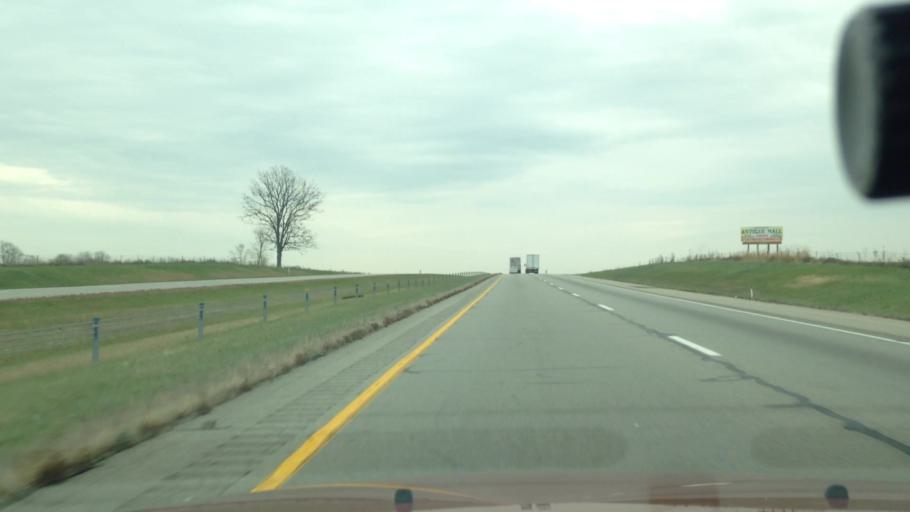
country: US
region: Indiana
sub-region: Wayne County
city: Cambridge City
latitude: 39.8532
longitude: -85.1922
